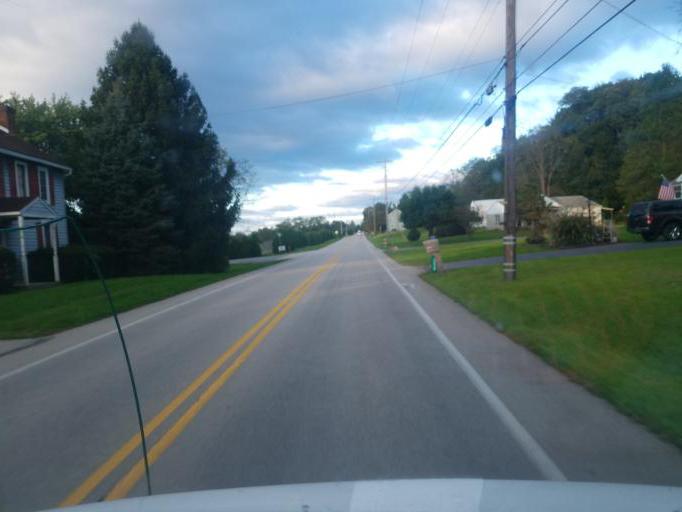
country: US
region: Pennsylvania
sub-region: York County
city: Weigelstown
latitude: 39.9435
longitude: -76.8414
